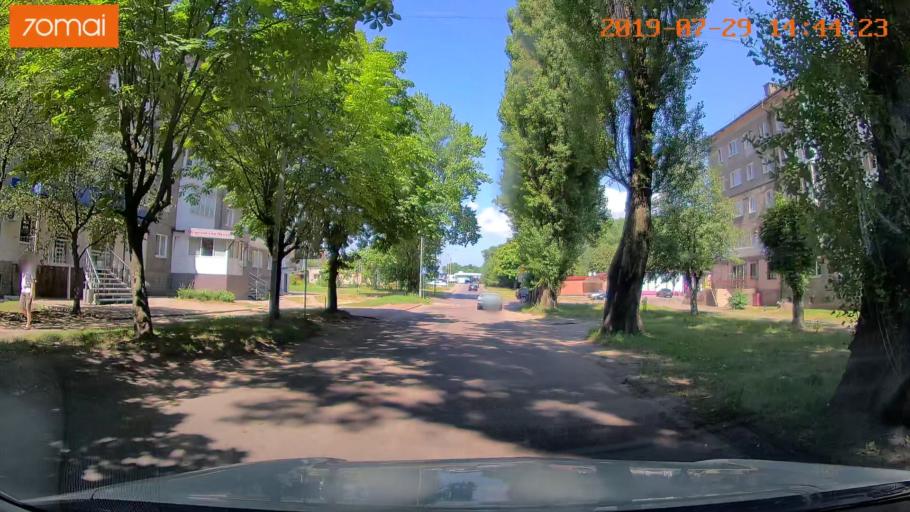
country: RU
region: Kaliningrad
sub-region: Gorod Kaliningrad
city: Baltiysk
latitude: 54.6620
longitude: 19.9088
